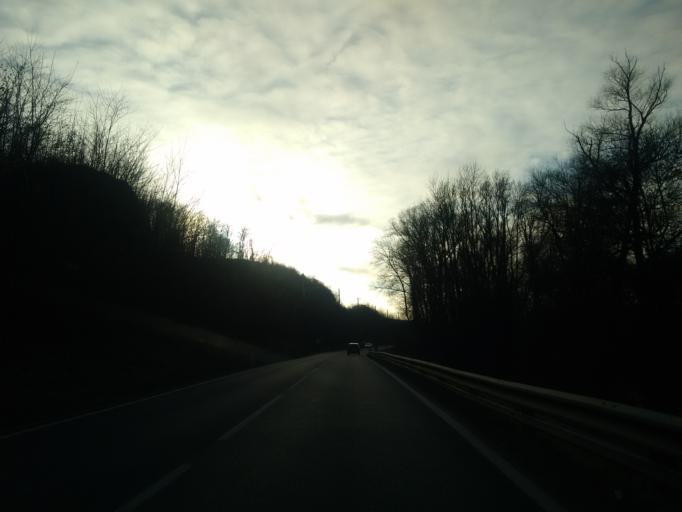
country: AT
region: Lower Austria
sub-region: Politischer Bezirk Melk
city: Melk
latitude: 48.2225
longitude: 15.3212
